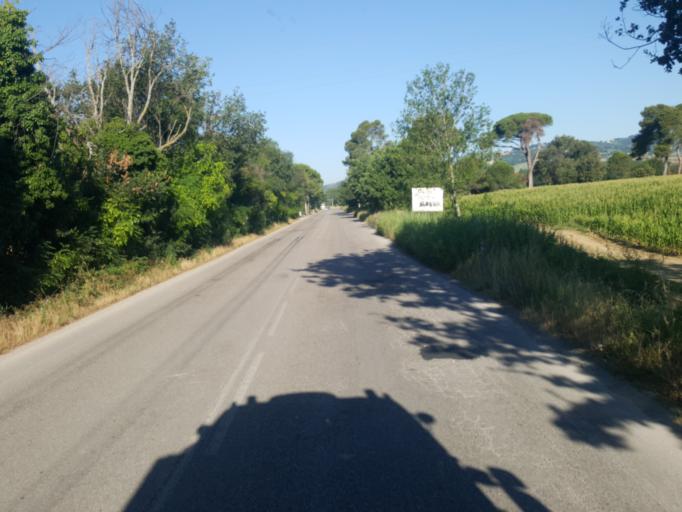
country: IT
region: The Marches
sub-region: Provincia di Pesaro e Urbino
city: Cappone
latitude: 43.8389
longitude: 12.7421
